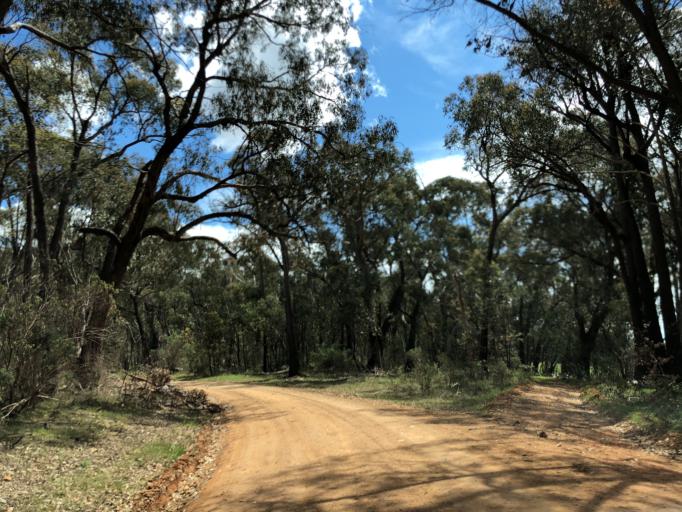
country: AU
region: Victoria
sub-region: Benalla
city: Benalla
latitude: -36.7332
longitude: 146.1477
